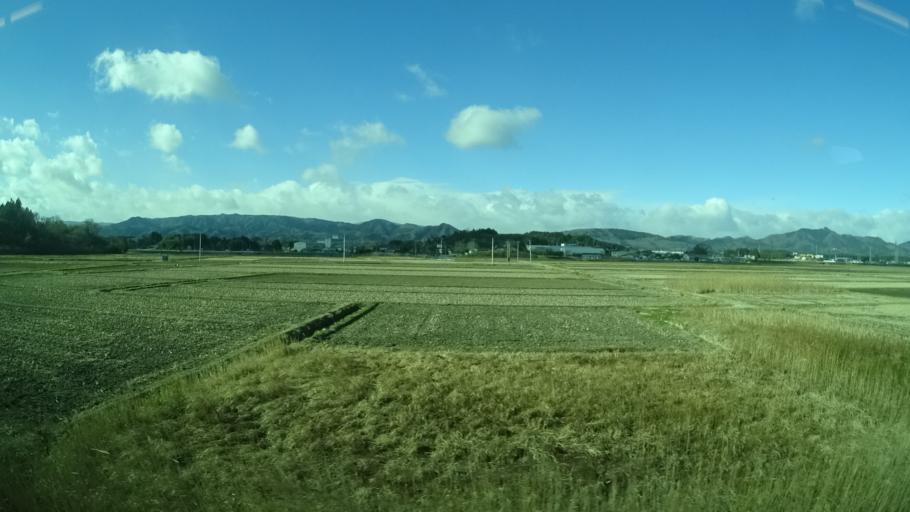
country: JP
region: Miyagi
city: Marumori
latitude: 37.8243
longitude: 140.9256
